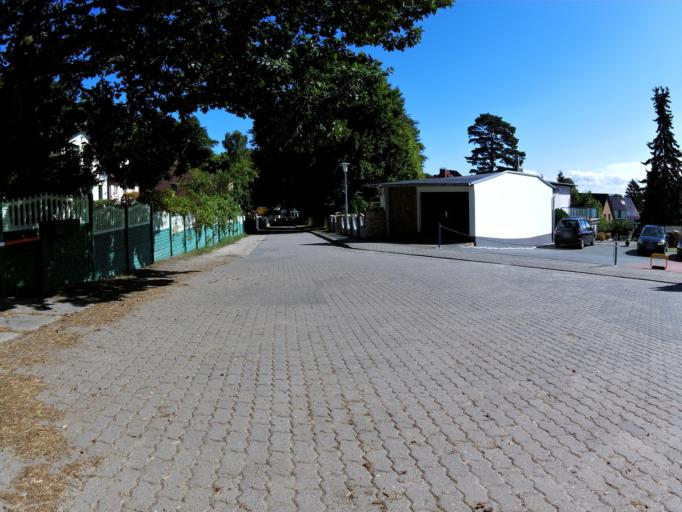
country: DE
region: Mecklenburg-Vorpommern
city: Seebad Bansin
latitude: 53.9716
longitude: 14.1377
